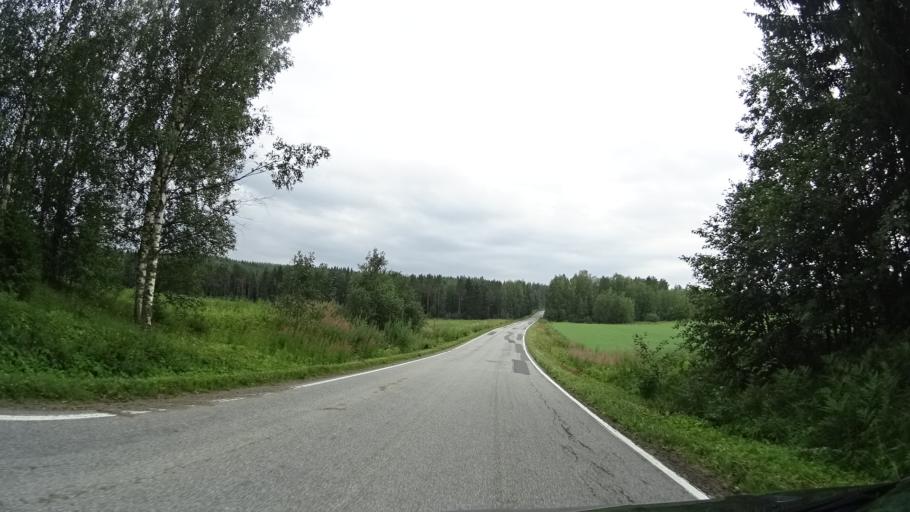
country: FI
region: Southern Savonia
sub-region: Savonlinna
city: Punkaharju
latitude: 61.7528
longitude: 29.5136
